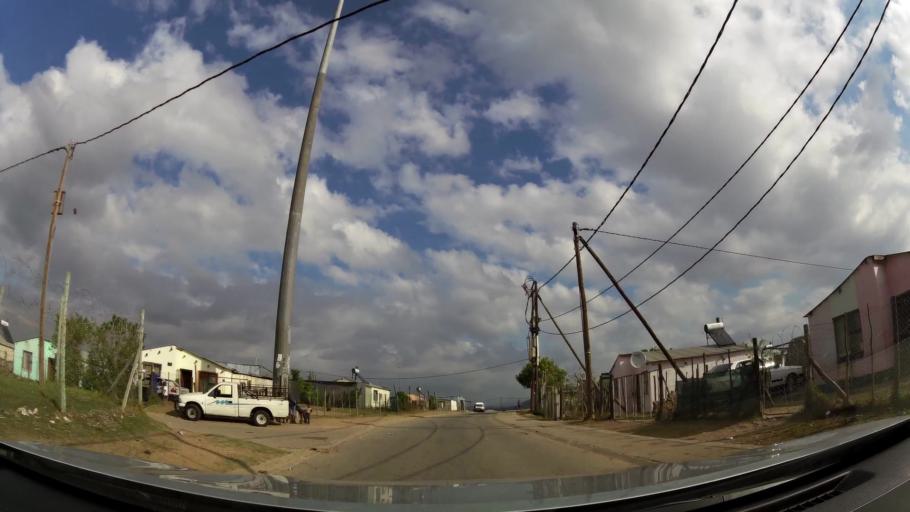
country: ZA
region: Eastern Cape
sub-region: Nelson Mandela Bay Metropolitan Municipality
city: Uitenhage
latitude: -33.7451
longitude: 25.3968
